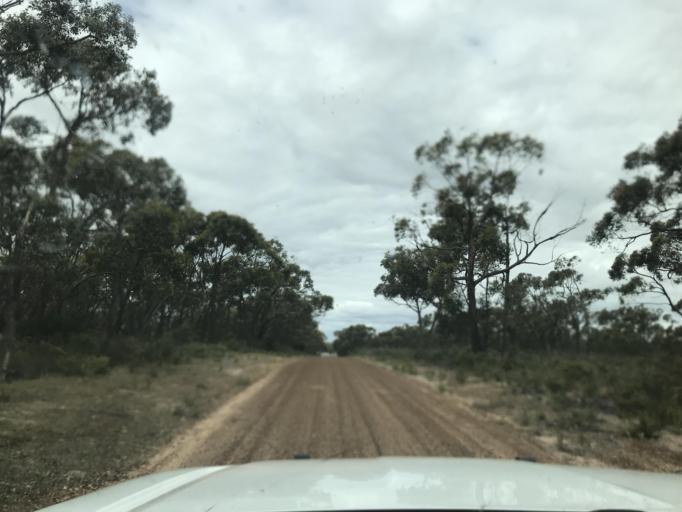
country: AU
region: South Australia
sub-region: Naracoorte and Lucindale
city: Naracoorte
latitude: -36.9224
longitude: 141.3285
